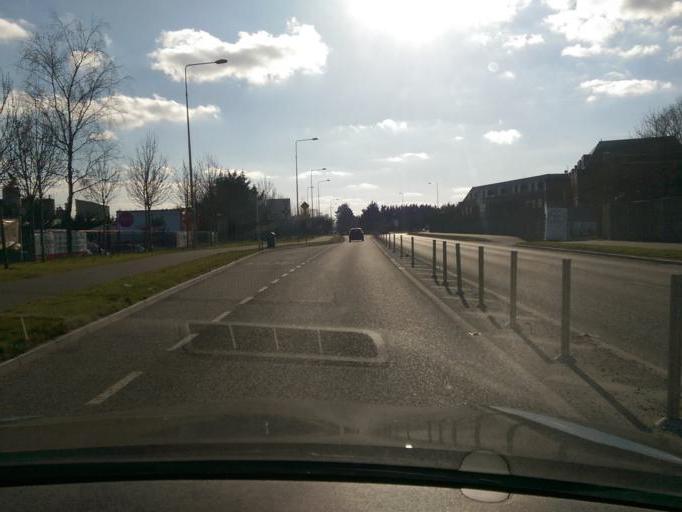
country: IE
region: Leinster
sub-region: Kildare
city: Johnstown
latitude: 53.2314
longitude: -6.6401
